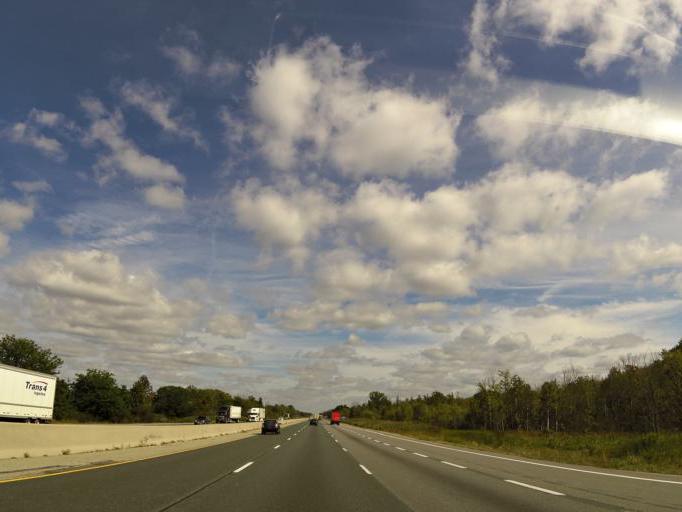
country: CA
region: Ontario
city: Dorchester
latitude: 42.9593
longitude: -81.0549
